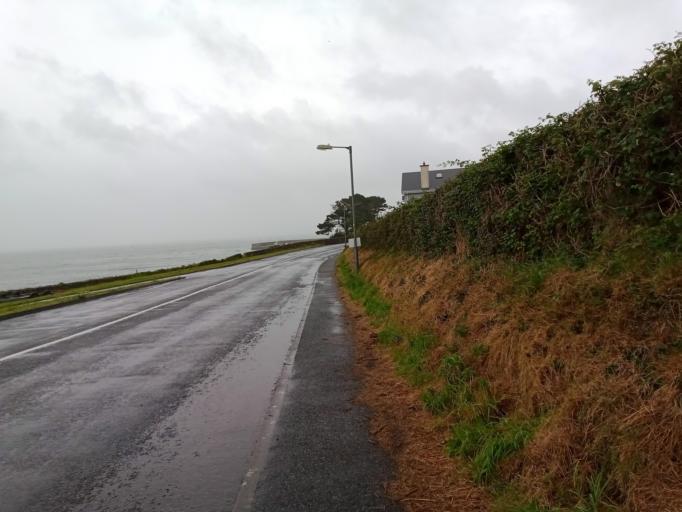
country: IE
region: Munster
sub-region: Waterford
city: Dungarvan
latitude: 52.0533
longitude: -7.5515
